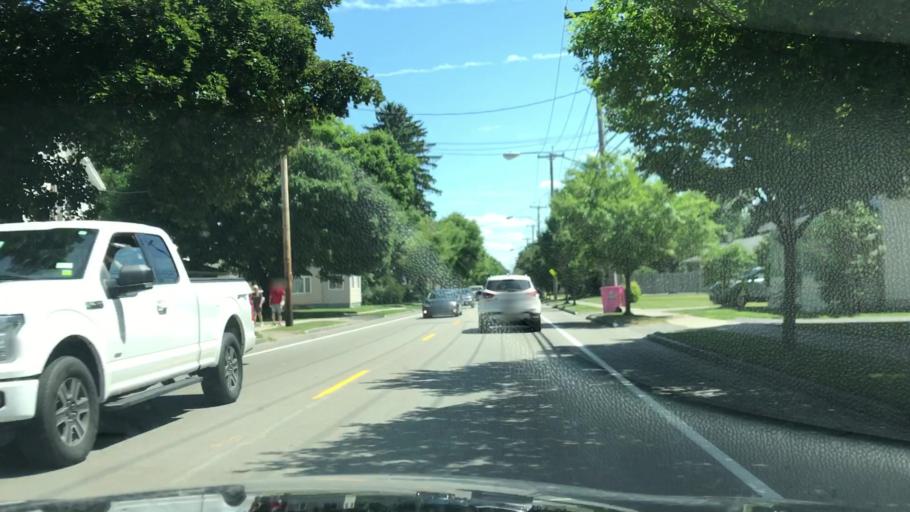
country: US
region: New York
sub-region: Livingston County
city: Mount Morris
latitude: 42.7347
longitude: -77.8795
